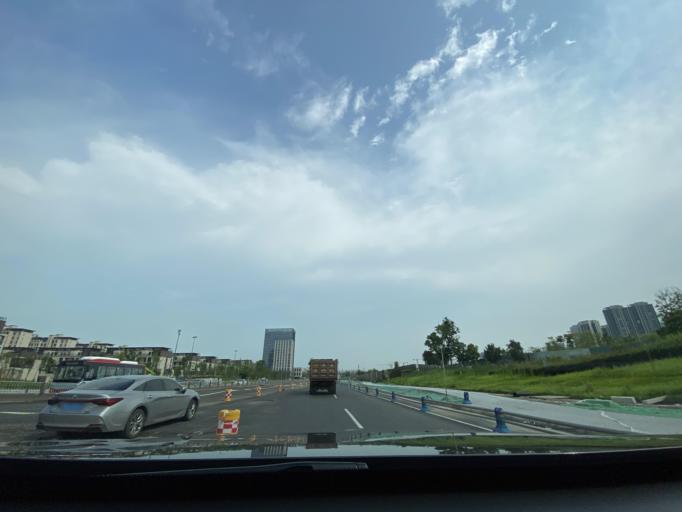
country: CN
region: Sichuan
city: Dongsheng
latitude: 30.4534
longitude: 104.0883
